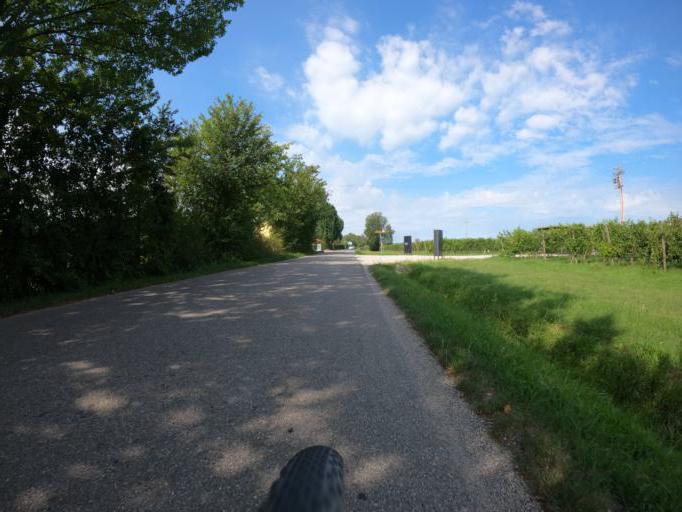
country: IT
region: Lombardy
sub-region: Provincia di Brescia
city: San Martino della Battaglia
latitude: 45.4424
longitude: 10.6126
